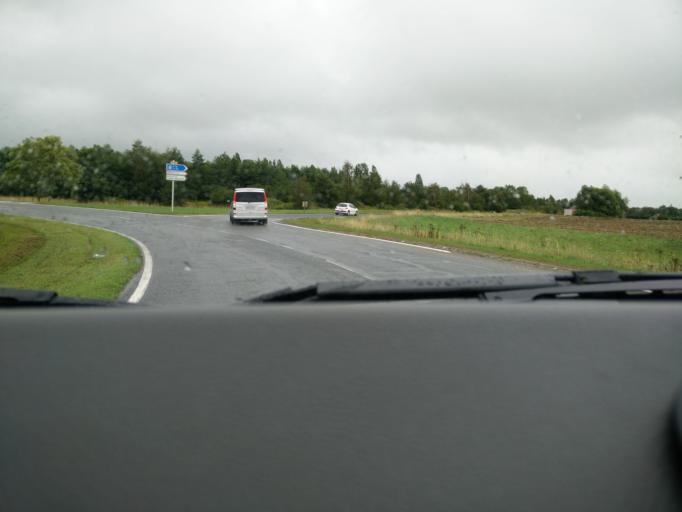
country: FR
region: Picardie
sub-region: Departement de la Somme
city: Rue
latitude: 50.2647
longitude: 1.6899
